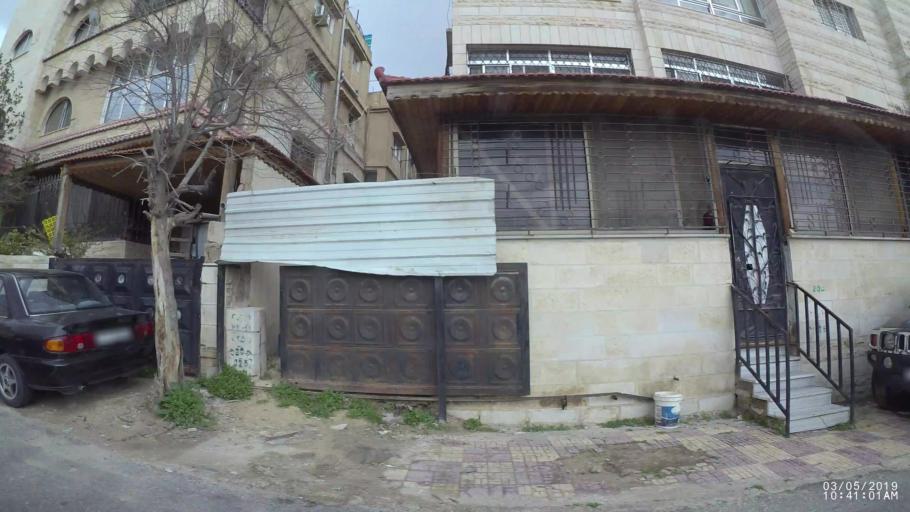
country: JO
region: Amman
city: Amman
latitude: 31.9815
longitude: 35.9215
